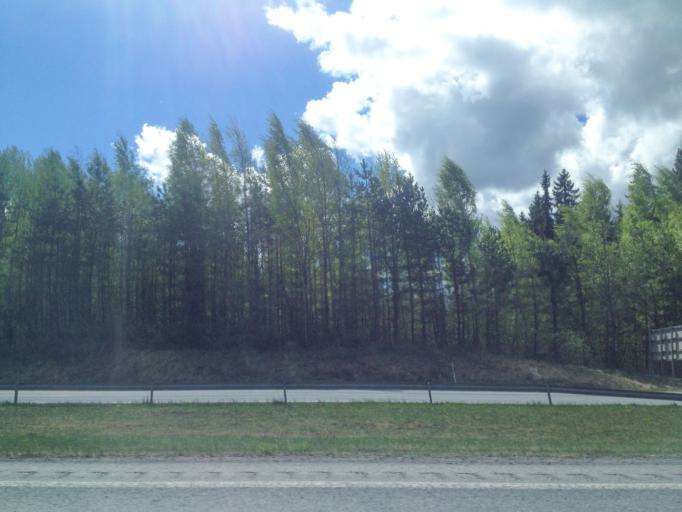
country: FI
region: Haeme
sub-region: Haemeenlinna
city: Parola
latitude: 61.0405
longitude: 24.3714
